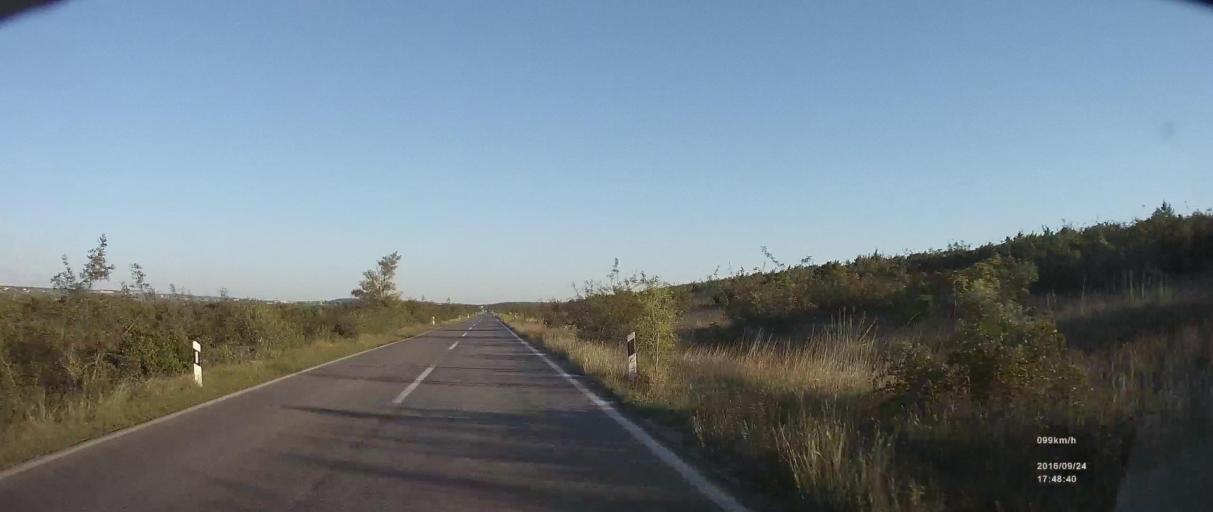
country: HR
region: Zadarska
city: Polaca
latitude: 44.0622
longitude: 15.5394
